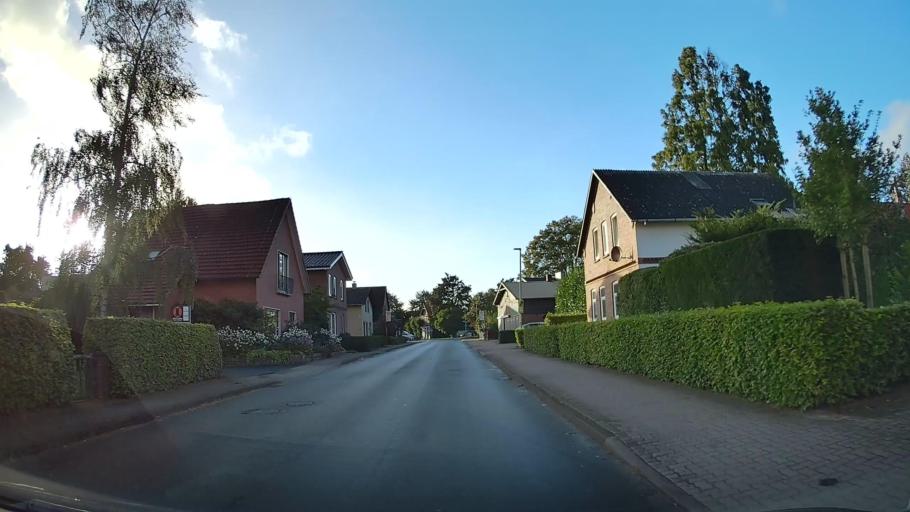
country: DE
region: Schleswig-Holstein
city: Horst
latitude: 53.8120
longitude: 9.6273
